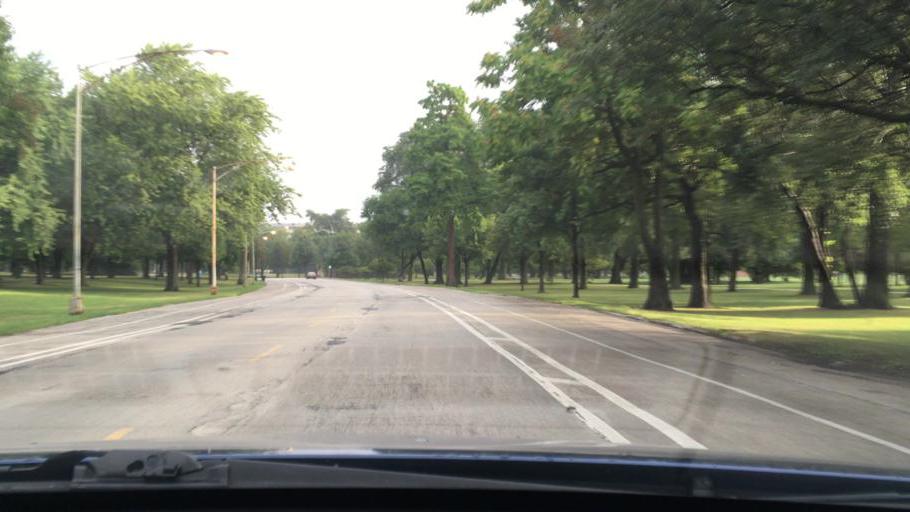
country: US
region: Illinois
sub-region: Cook County
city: Chicago
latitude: 41.7973
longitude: -87.6142
